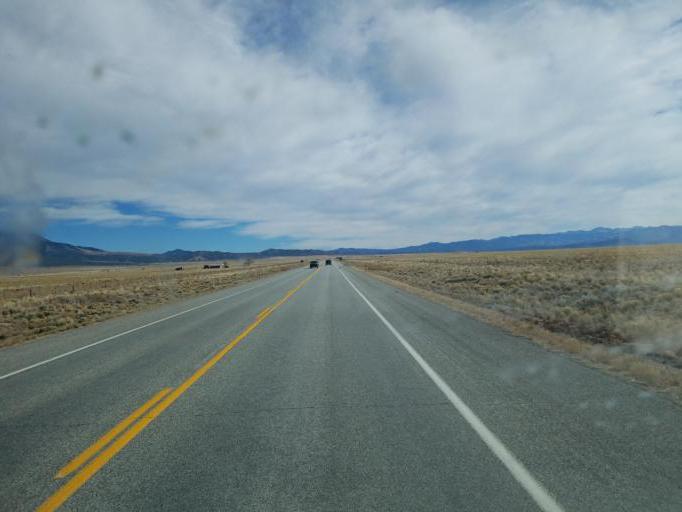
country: US
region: Colorado
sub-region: Alamosa County
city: Alamosa East
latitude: 37.4749
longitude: -105.6100
